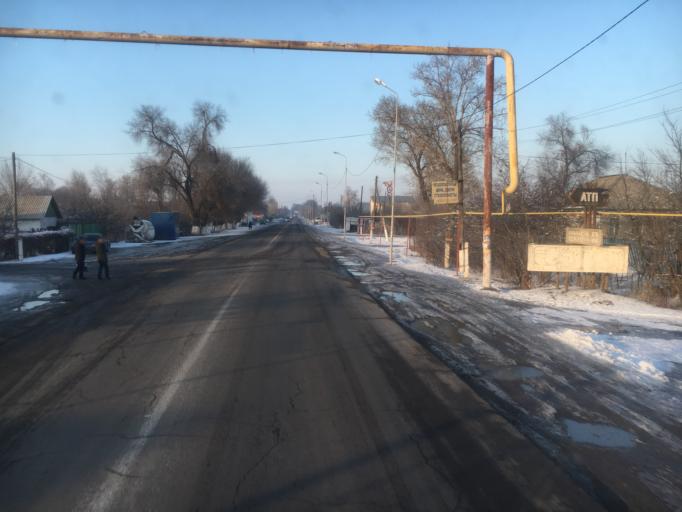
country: KZ
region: Almaty Oblysy
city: Burunday
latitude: 43.3674
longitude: 76.6413
